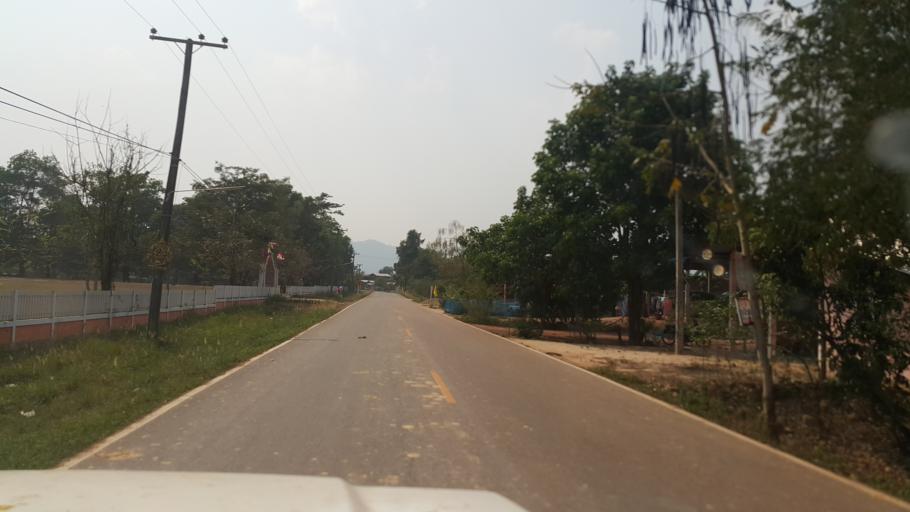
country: TH
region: Nakhon Phanom
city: Ban Phaeng
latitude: 17.9594
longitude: 104.1824
